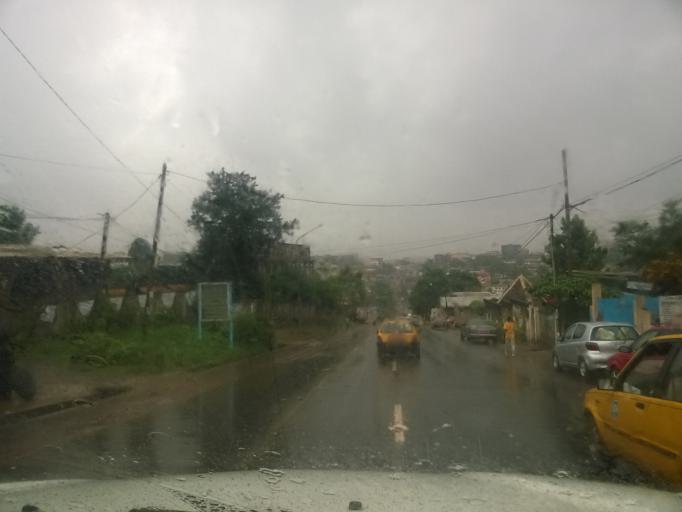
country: CM
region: Centre
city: Yaounde
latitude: 3.8801
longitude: 11.5392
